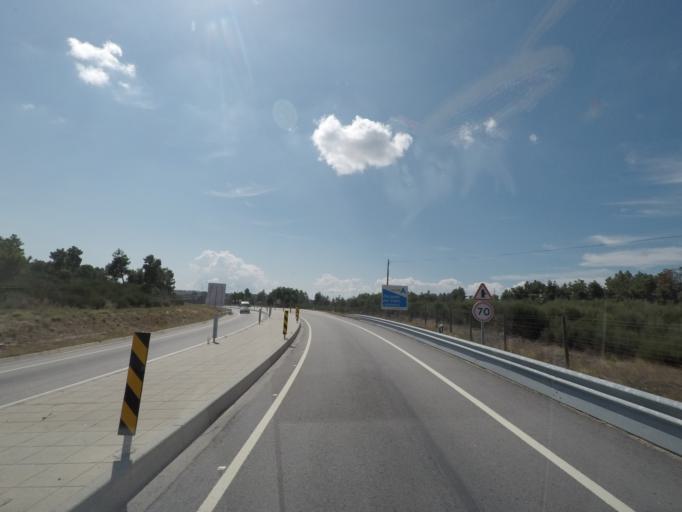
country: PT
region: Vila Real
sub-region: Murca
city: Murca
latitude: 41.3395
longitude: -7.4702
